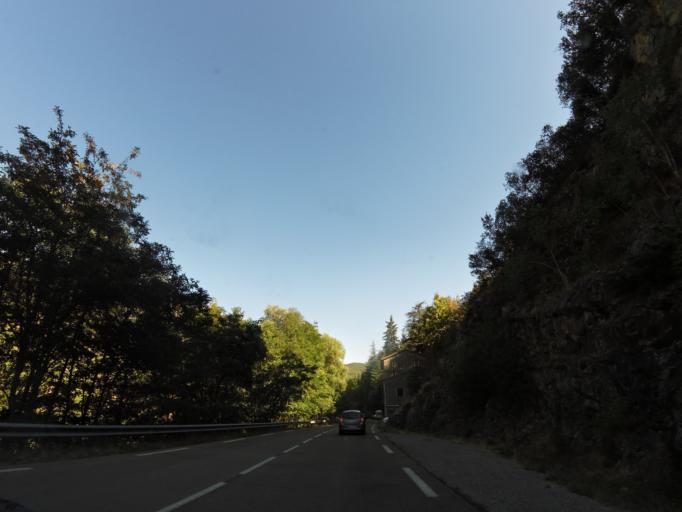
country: FR
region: Languedoc-Roussillon
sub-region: Departement du Gard
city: Valleraugue
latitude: 44.0546
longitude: 3.6864
